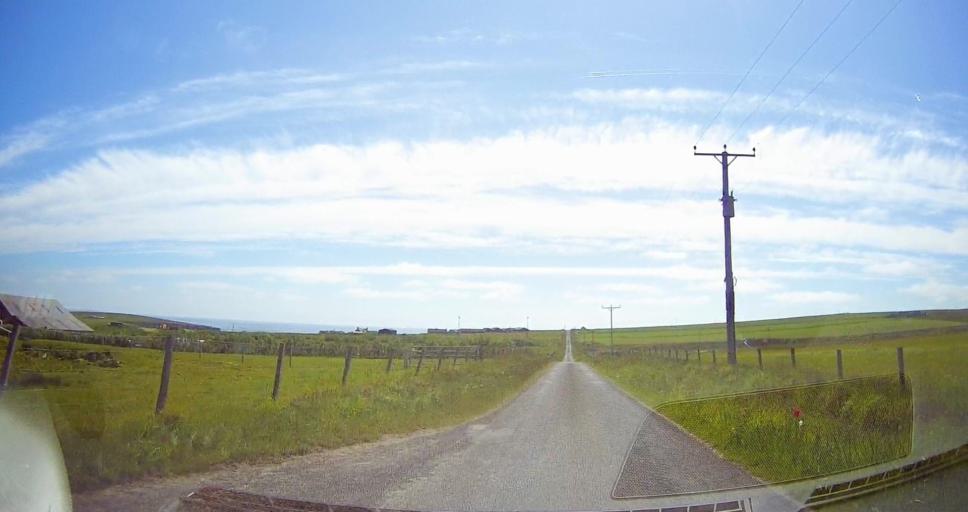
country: GB
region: Scotland
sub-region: Orkney Islands
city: Kirkwall
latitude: 58.8259
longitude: -2.9106
